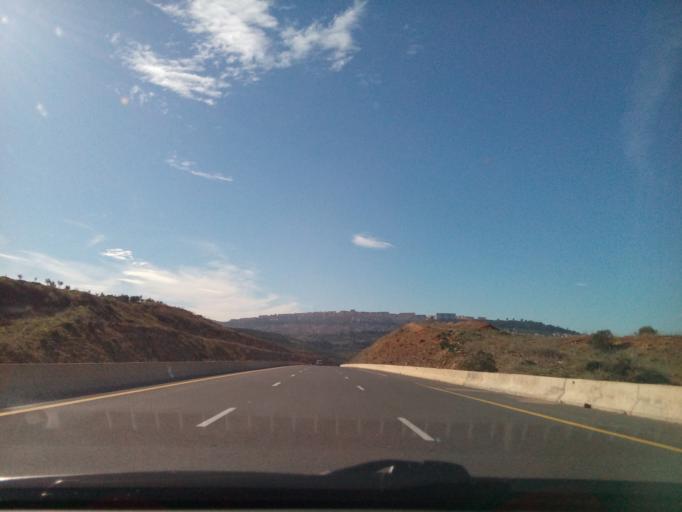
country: DZ
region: Tlemcen
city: Chetouane
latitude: 34.9459
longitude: -1.3078
